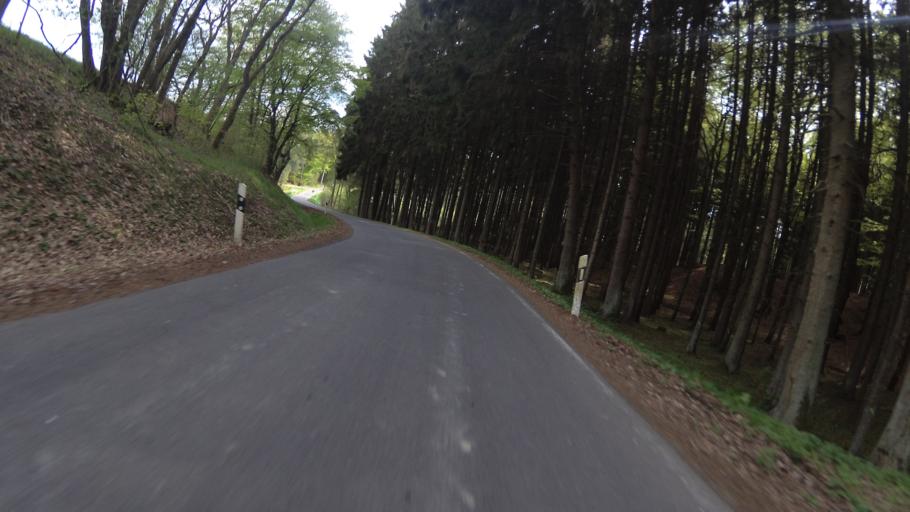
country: DE
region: Rheinland-Pfalz
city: Welcherath
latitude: 50.3303
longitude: 6.9666
